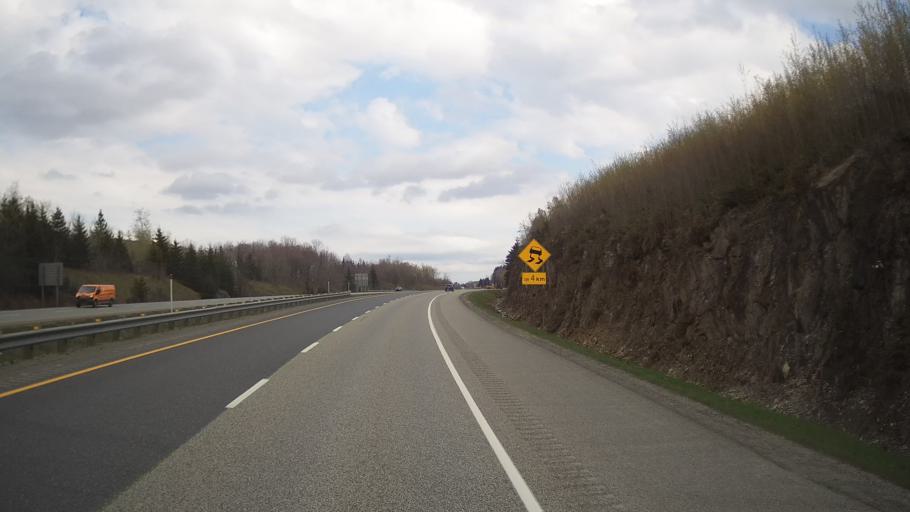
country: CA
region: Quebec
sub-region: Estrie
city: Magog
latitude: 45.2974
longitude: -72.3049
